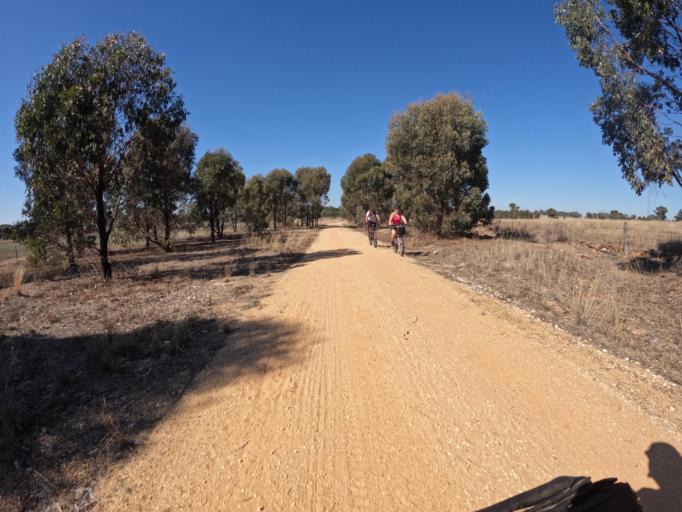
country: AU
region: Victoria
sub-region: Greater Bendigo
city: Kennington
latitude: -36.8226
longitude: 144.5802
